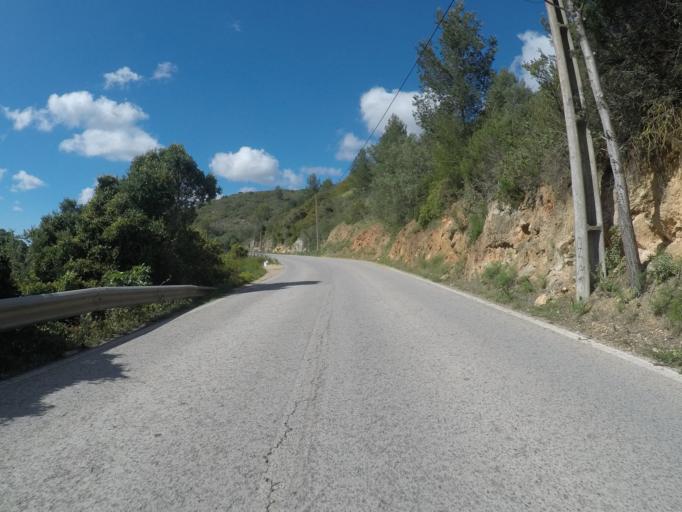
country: PT
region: Faro
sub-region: Vila do Bispo
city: Vila do Bispo
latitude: 37.0683
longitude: -8.8249
